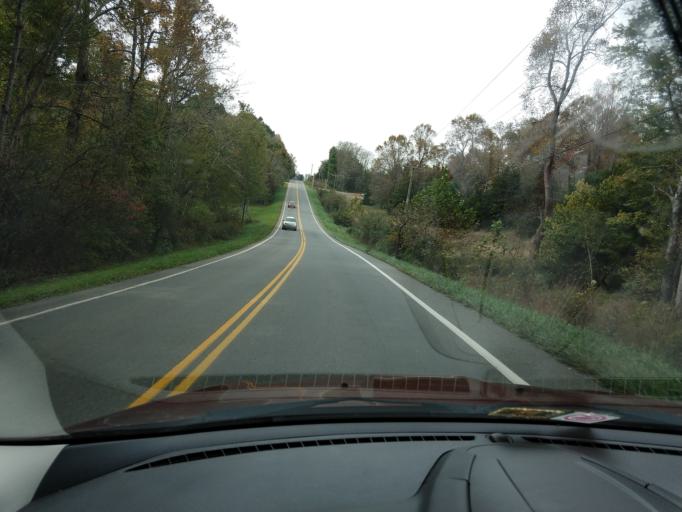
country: US
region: Virginia
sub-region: Franklin County
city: Union Hall
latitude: 36.9892
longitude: -79.7261
